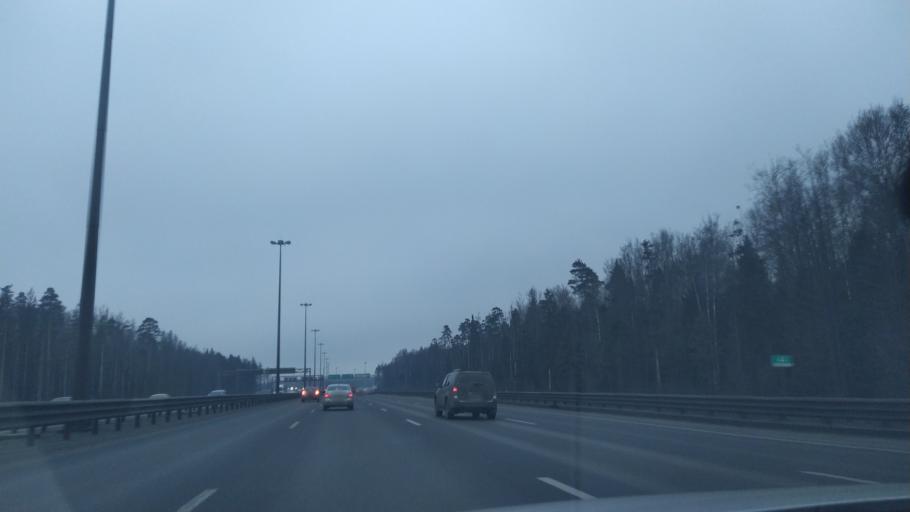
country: RU
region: Leningrad
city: Yanino Vtoroye
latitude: 59.9543
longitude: 30.5484
